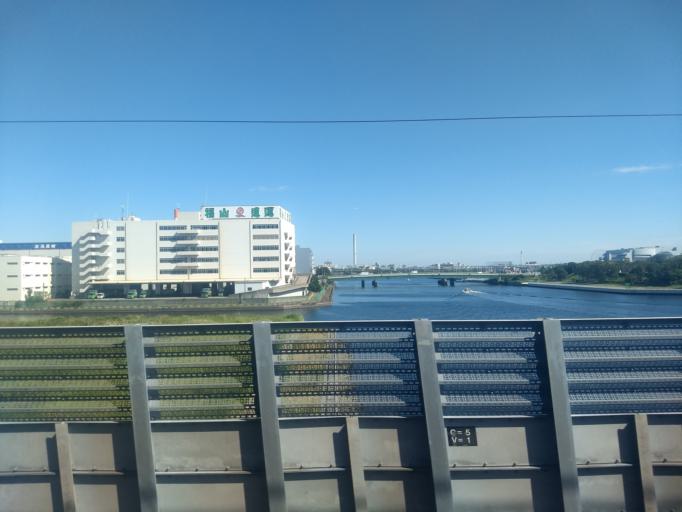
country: JP
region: Tokyo
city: Urayasu
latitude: 35.6553
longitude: 139.8192
